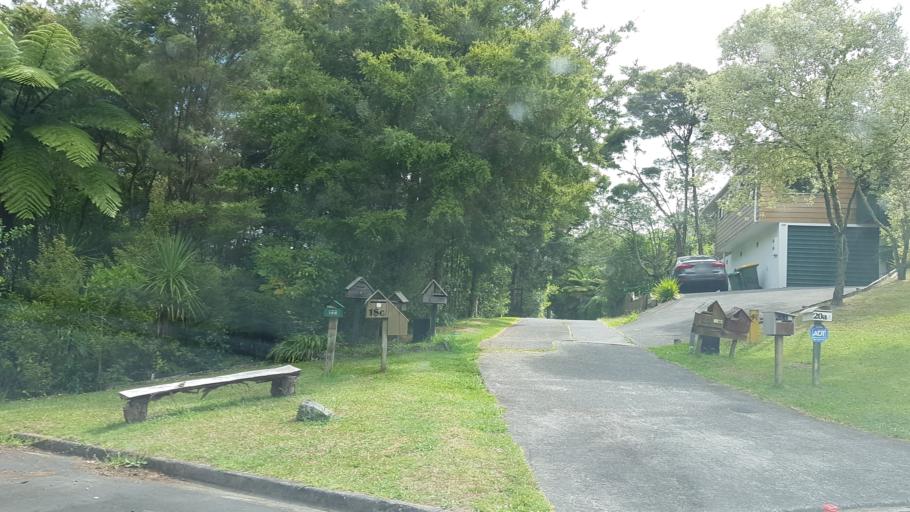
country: NZ
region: Auckland
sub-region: Auckland
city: North Shore
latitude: -36.7697
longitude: 174.7168
